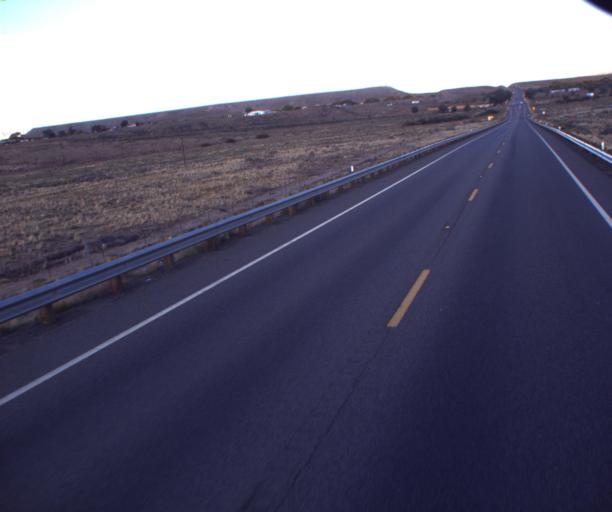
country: US
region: New Mexico
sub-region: San Juan County
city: Shiprock
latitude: 36.9269
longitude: -109.0981
